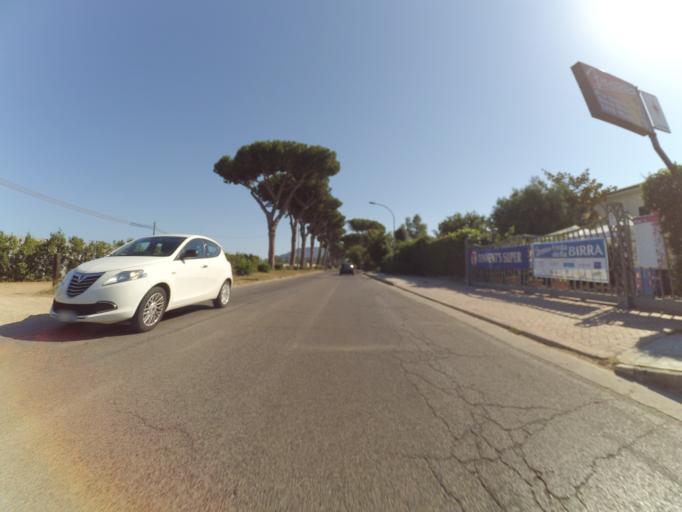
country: IT
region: Latium
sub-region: Provincia di Latina
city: San Felice Circeo
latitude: 41.2708
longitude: 13.0977
